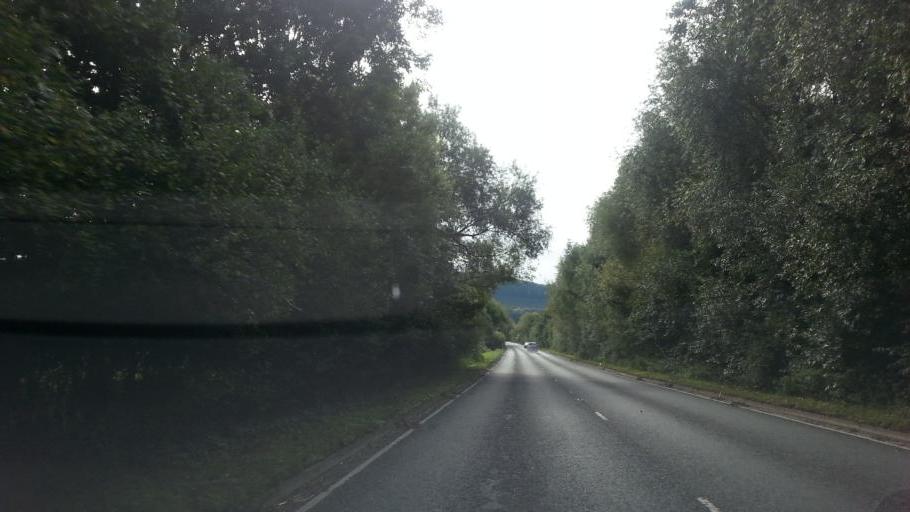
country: GB
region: England
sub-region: Herefordshire
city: Ross on Wye
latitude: 51.9192
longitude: -2.5706
